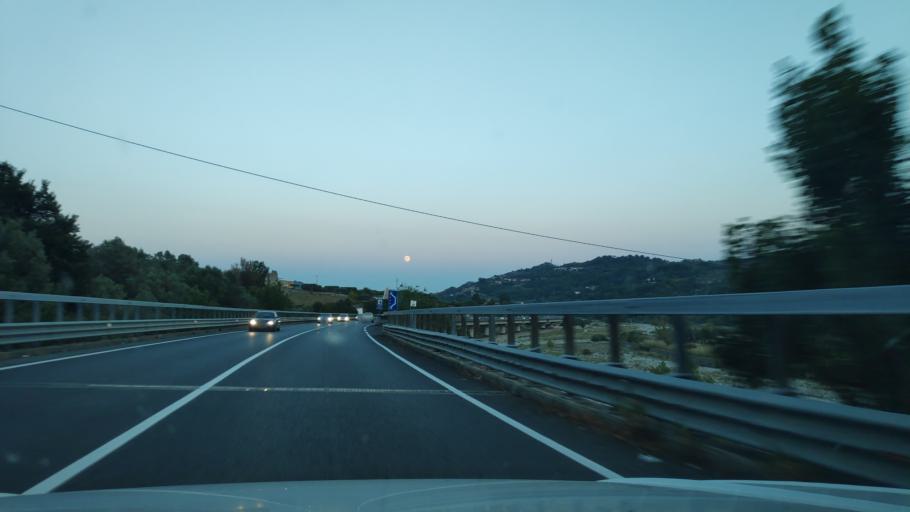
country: IT
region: Calabria
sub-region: Provincia di Reggio Calabria
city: Mammola
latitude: 38.3503
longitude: 16.2527
